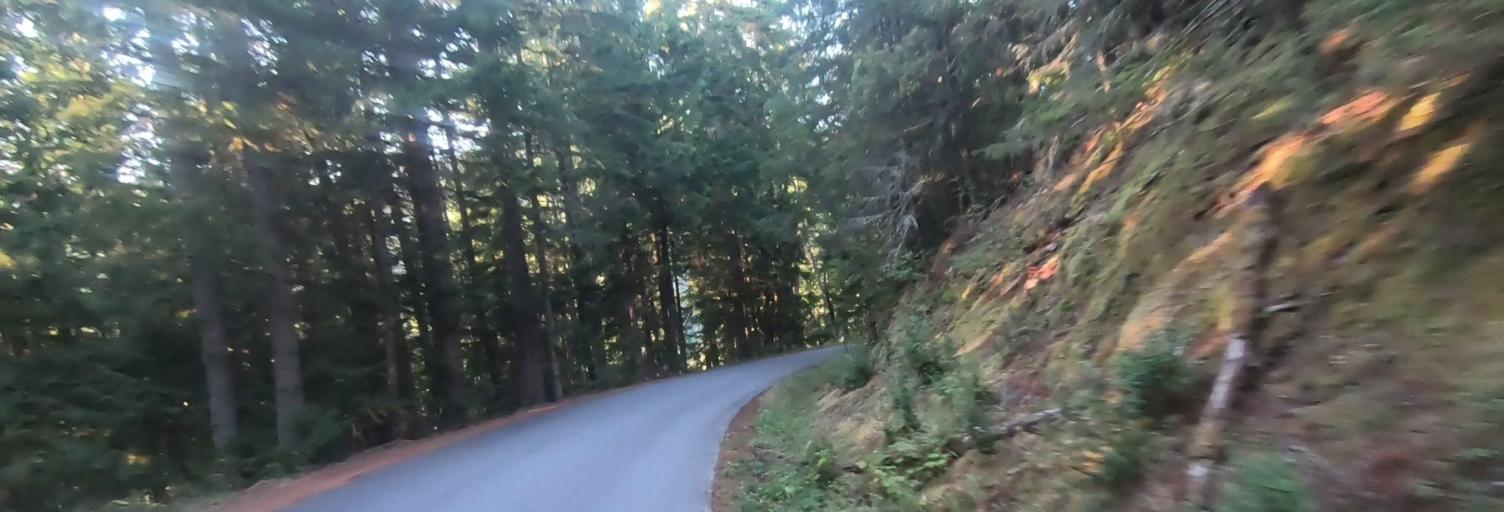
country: US
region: Washington
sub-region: Whatcom County
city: Peaceful Valley
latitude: 48.9163
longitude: -121.9730
